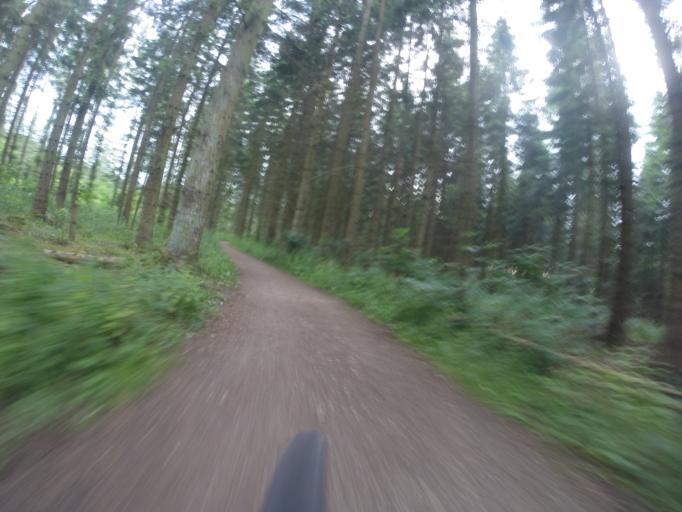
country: DK
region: Capital Region
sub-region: Ballerup Kommune
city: Ballerup
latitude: 55.6989
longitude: 12.3378
